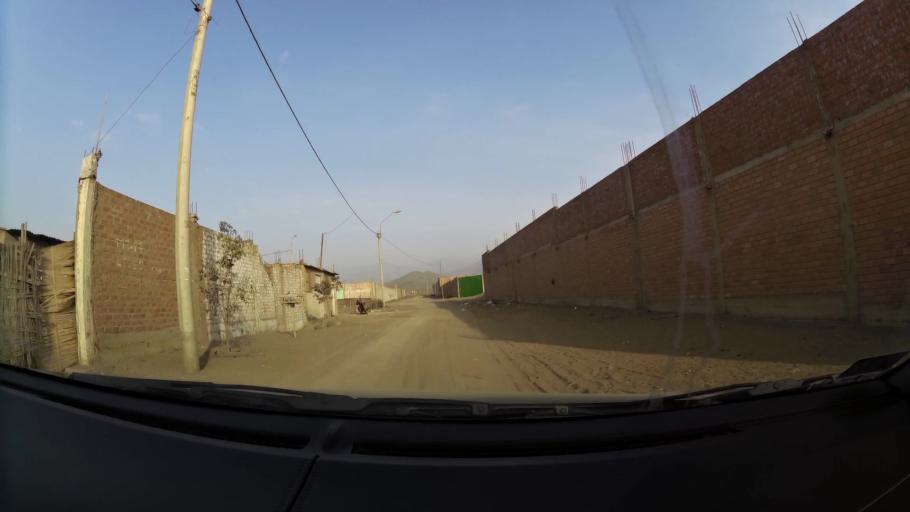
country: PE
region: Lima
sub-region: Lima
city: Santa Rosa
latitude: -11.7497
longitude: -77.1487
